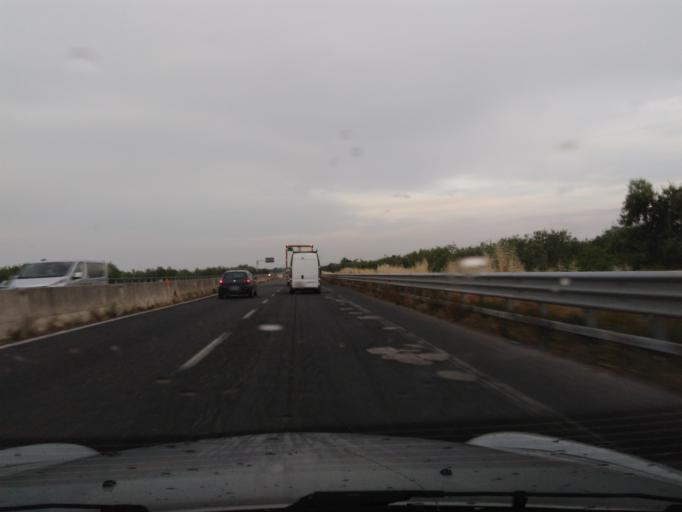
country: IT
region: Apulia
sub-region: Provincia di Bari
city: Molfetta
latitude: 41.1881
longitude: 16.6211
